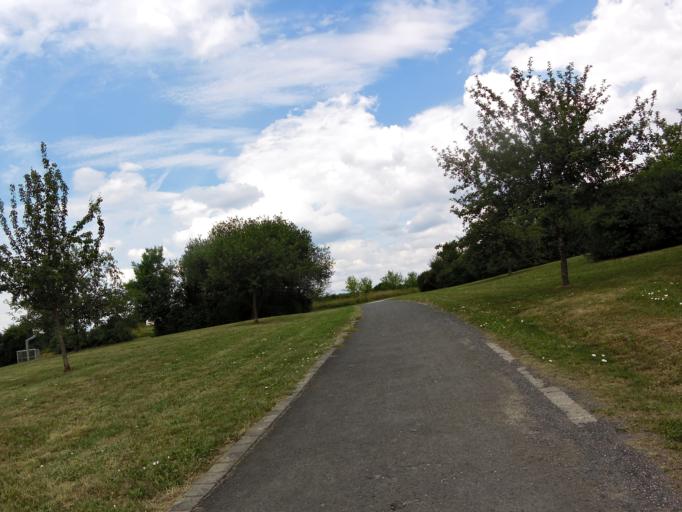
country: DE
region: Bavaria
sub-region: Regierungsbezirk Unterfranken
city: Eibelstadt
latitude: 49.7235
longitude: 9.9601
